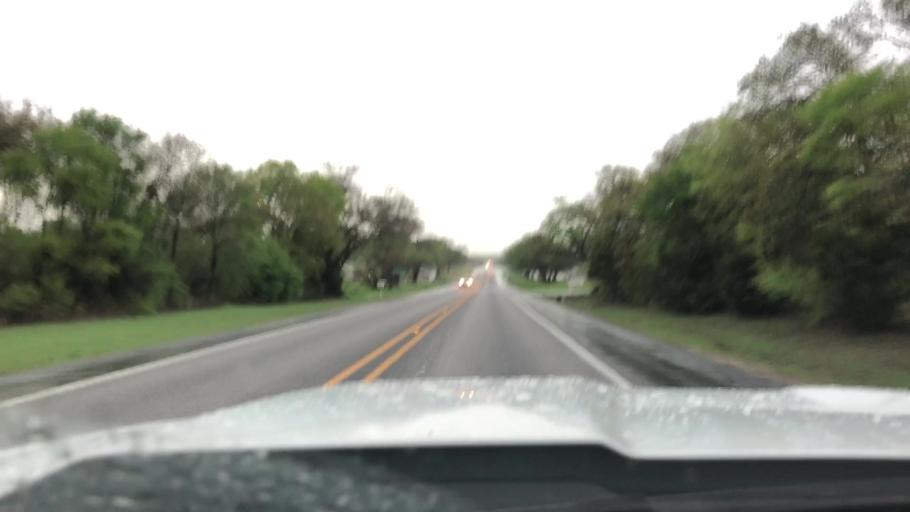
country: US
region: Texas
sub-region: Johnson County
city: Keene
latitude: 32.4044
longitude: -97.3263
